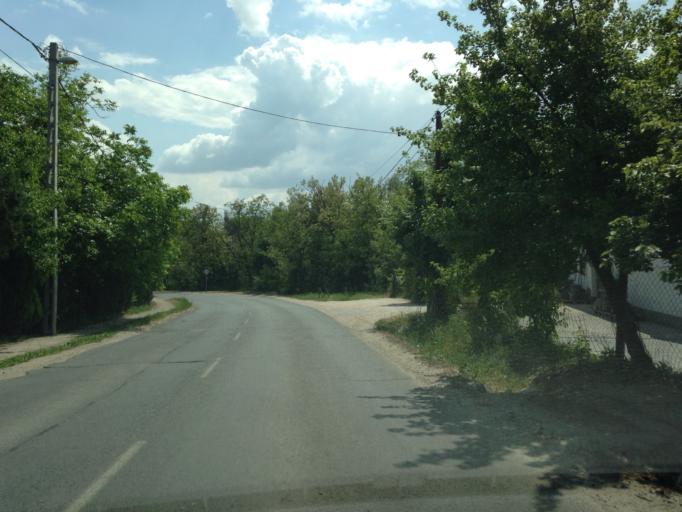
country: HU
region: Pest
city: Szentendre
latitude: 47.6818
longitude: 19.0627
